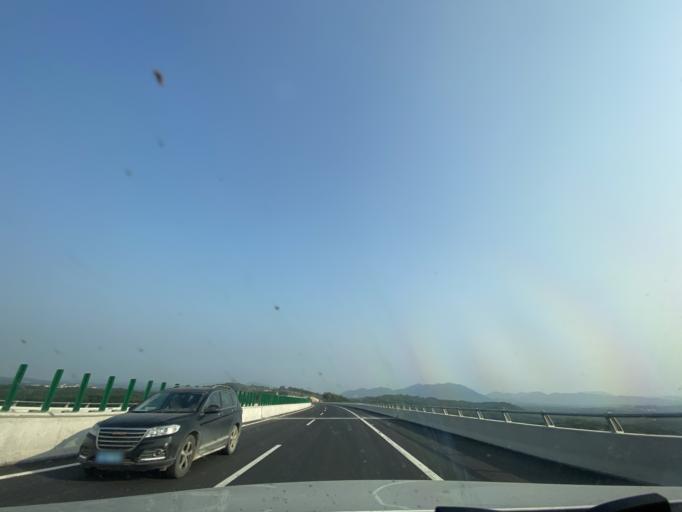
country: CN
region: Hainan
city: Xiangshui
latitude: 18.6359
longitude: 109.6309
